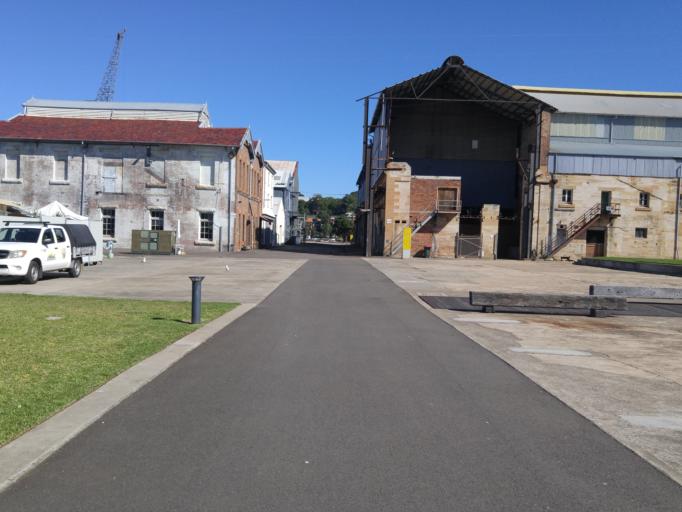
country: AU
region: New South Wales
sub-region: Lane Cove
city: Greenwich
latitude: -33.8471
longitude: 151.1736
